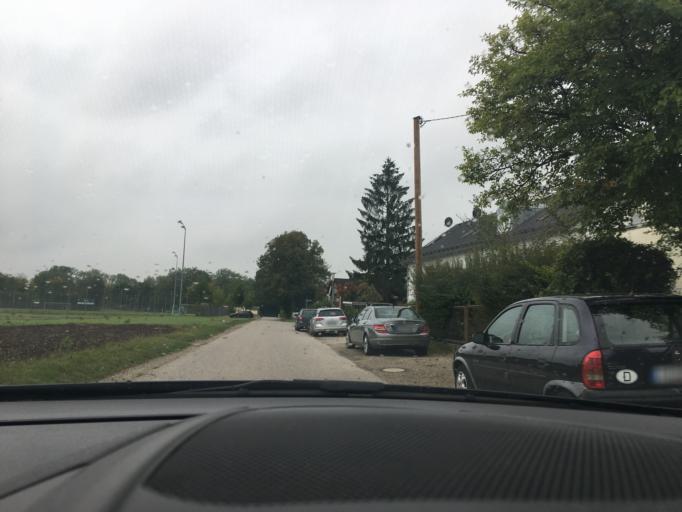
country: DE
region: Bavaria
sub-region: Upper Bavaria
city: Ismaning
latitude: 48.2535
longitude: 11.6997
